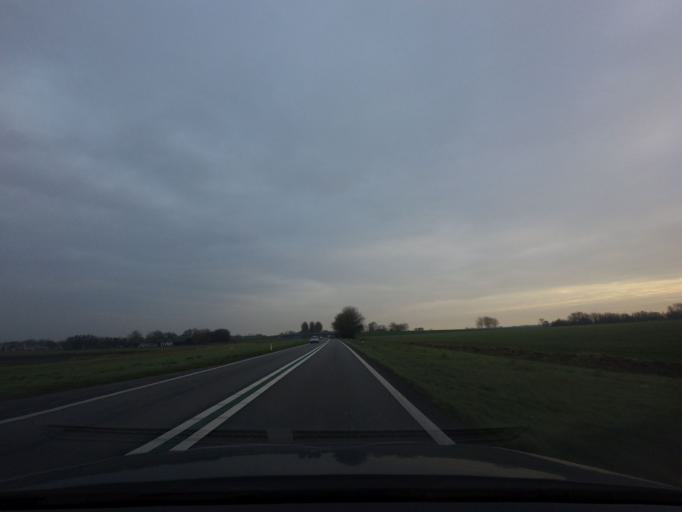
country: NL
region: North Holland
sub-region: Gemeente Opmeer
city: Opmeer
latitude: 52.7286
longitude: 4.8877
